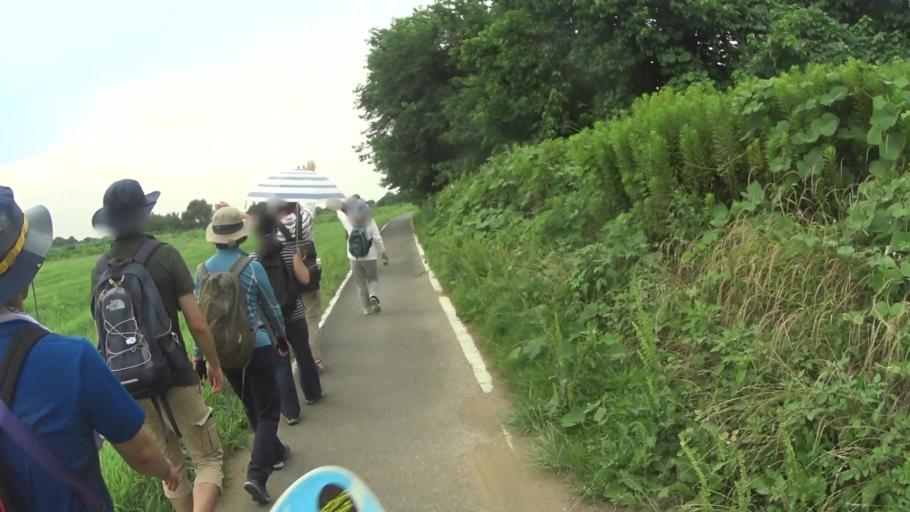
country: JP
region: Saitama
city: Okegawa
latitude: 35.9560
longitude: 139.5426
